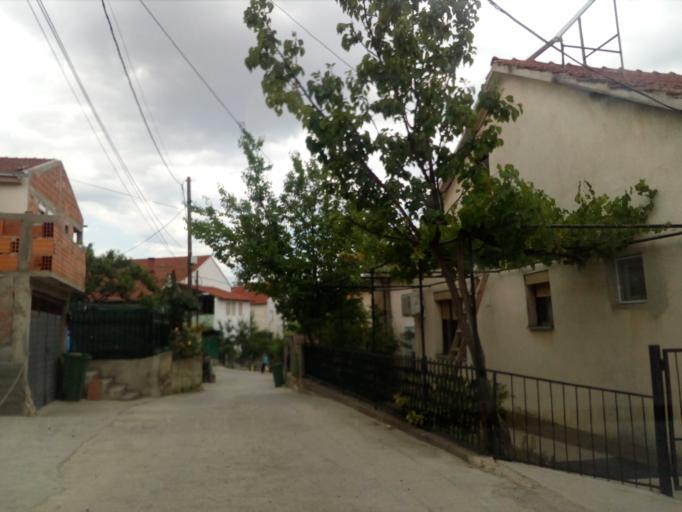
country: MK
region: Veles
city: Veles
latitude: 41.7086
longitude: 21.7599
